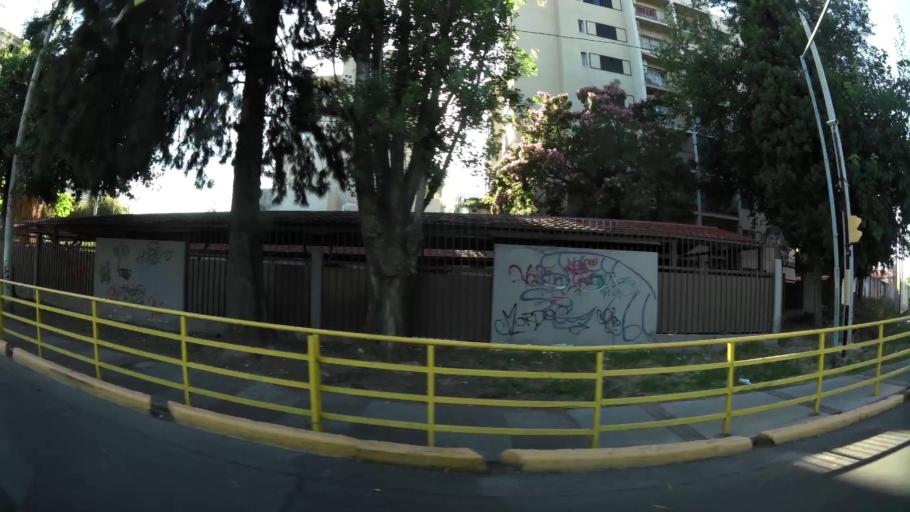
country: AR
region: Mendoza
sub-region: Departamento de Godoy Cruz
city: Godoy Cruz
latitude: -32.9114
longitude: -68.8505
